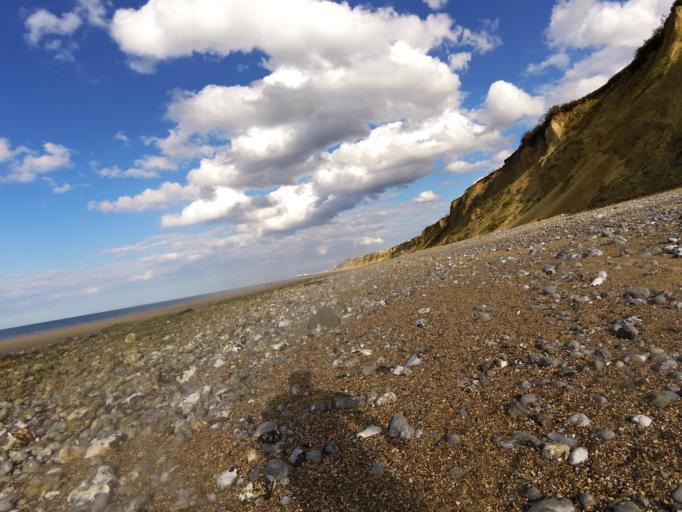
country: GB
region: England
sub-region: Norfolk
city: Cromer
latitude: 52.9385
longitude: 1.2709
